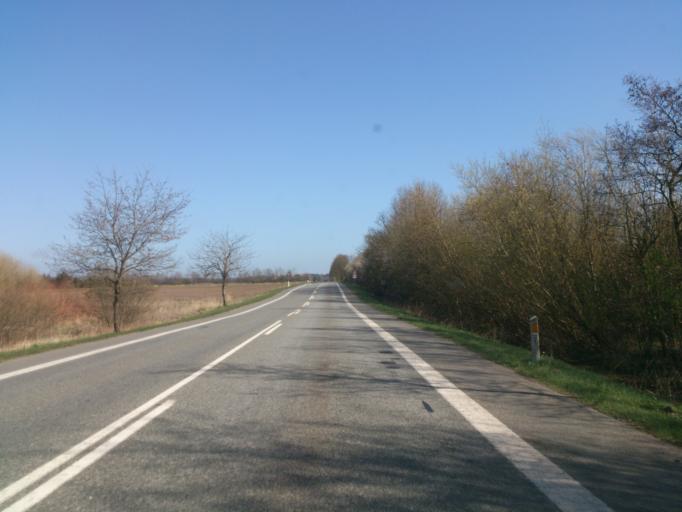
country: DK
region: Central Jutland
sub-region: Favrskov Kommune
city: Ulstrup
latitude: 56.4480
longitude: 9.7340
